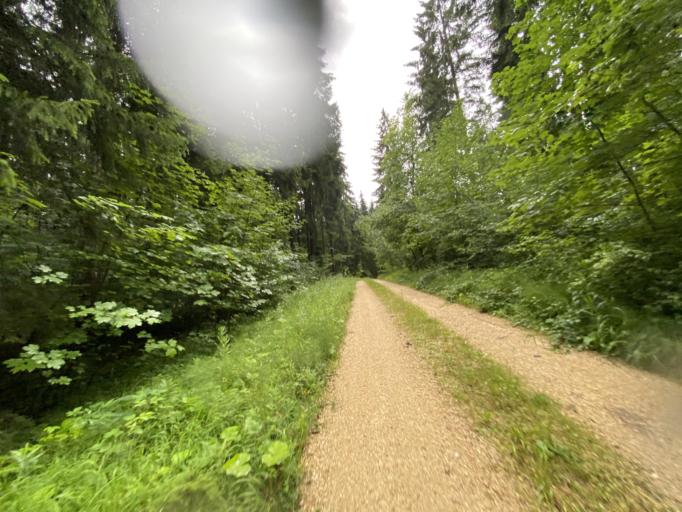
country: DE
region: Baden-Wuerttemberg
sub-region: Tuebingen Region
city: Sigmaringen
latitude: 48.1184
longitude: 9.2341
